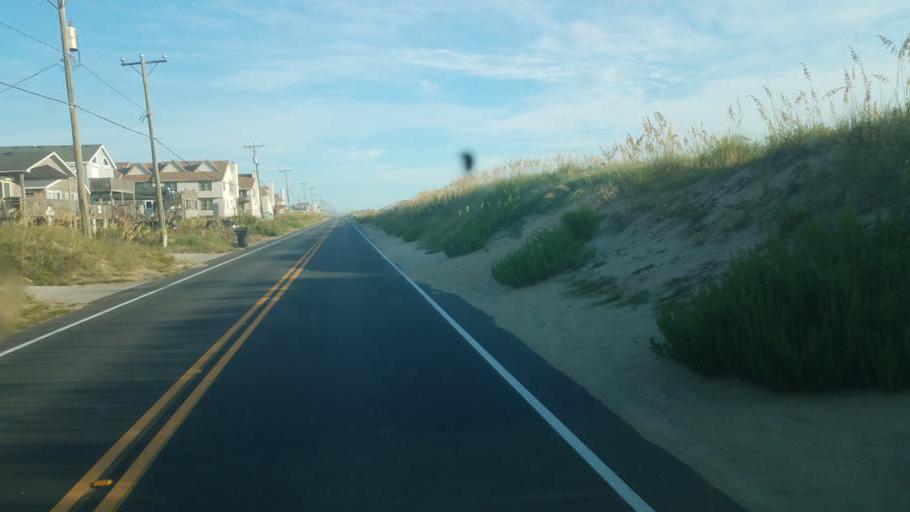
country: US
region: North Carolina
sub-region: Dare County
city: Kitty Hawk
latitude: 36.0641
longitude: -75.6886
